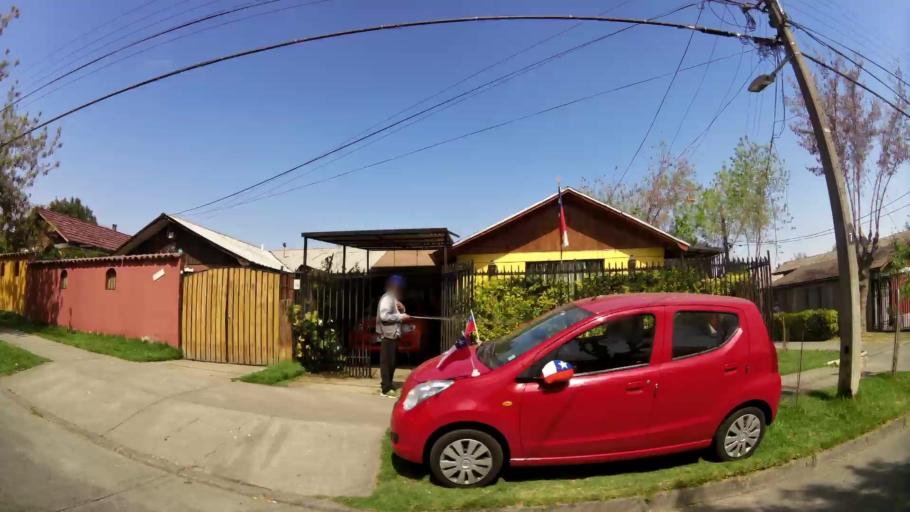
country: CL
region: Santiago Metropolitan
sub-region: Provincia de Santiago
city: Villa Presidente Frei, Nunoa, Santiago, Chile
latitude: -33.4647
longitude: -70.5432
